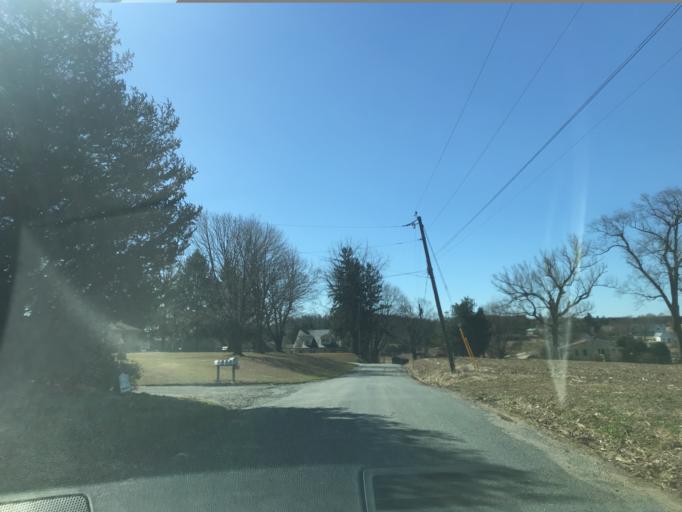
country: US
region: Pennsylvania
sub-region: York County
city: Stewartstown
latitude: 39.7172
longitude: -76.5248
